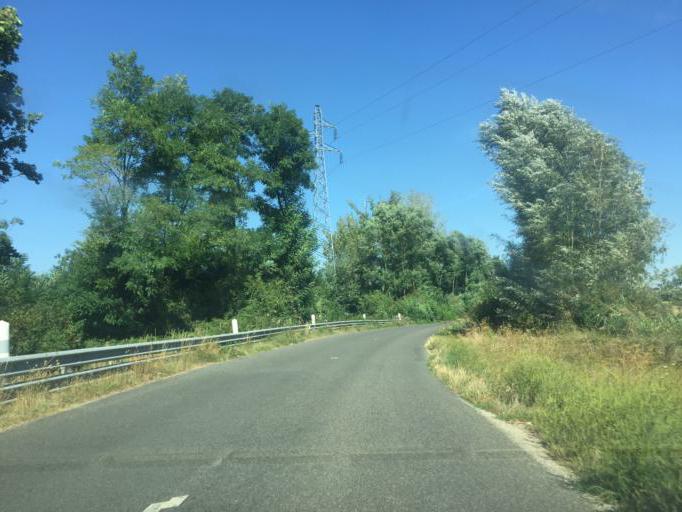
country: FR
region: Rhone-Alpes
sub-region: Departement de l'Ain
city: Tramoyes
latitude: 45.8855
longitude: 4.9688
